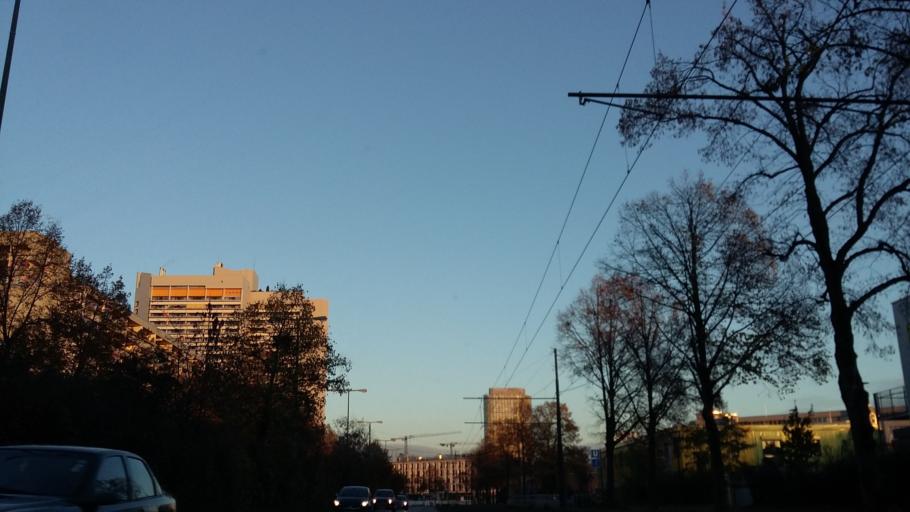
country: DE
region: Bavaria
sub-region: Upper Bavaria
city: Munich
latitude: 48.1347
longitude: 11.5190
